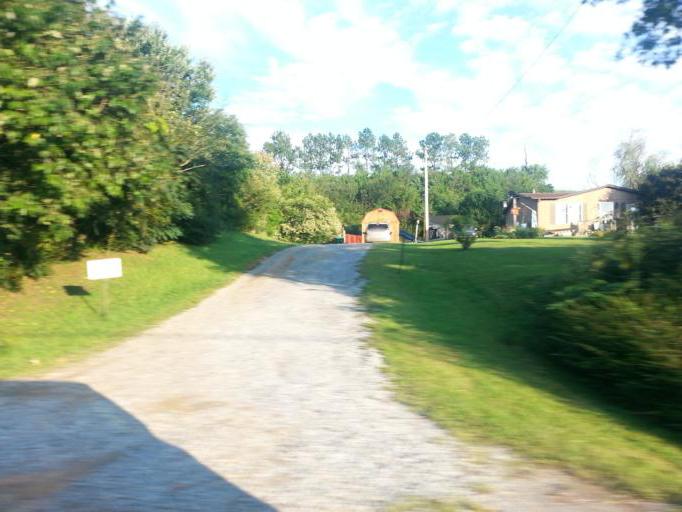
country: US
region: Tennessee
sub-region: Knox County
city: Mascot
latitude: 36.0429
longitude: -83.8139
